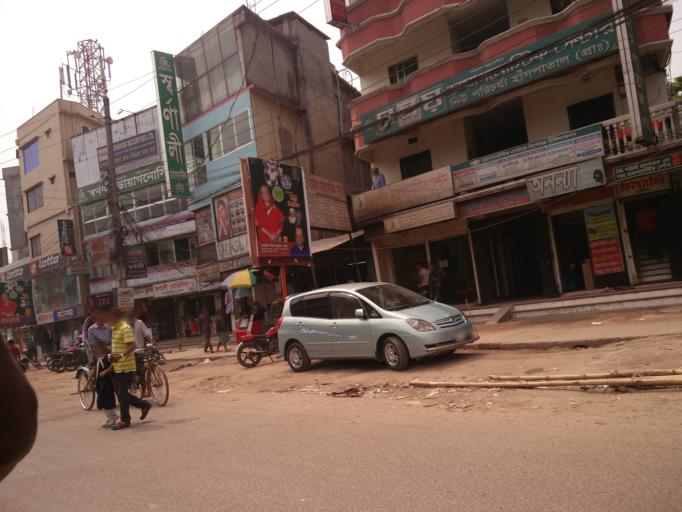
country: BD
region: Dhaka
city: Mymensingh
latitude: 24.7471
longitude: 90.4087
